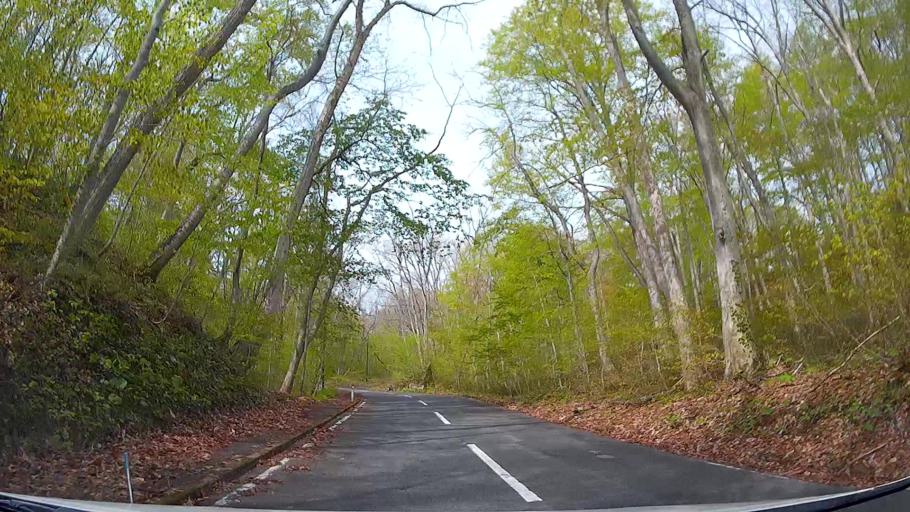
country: JP
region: Akita
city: Hanawa
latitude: 40.4319
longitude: 140.9152
